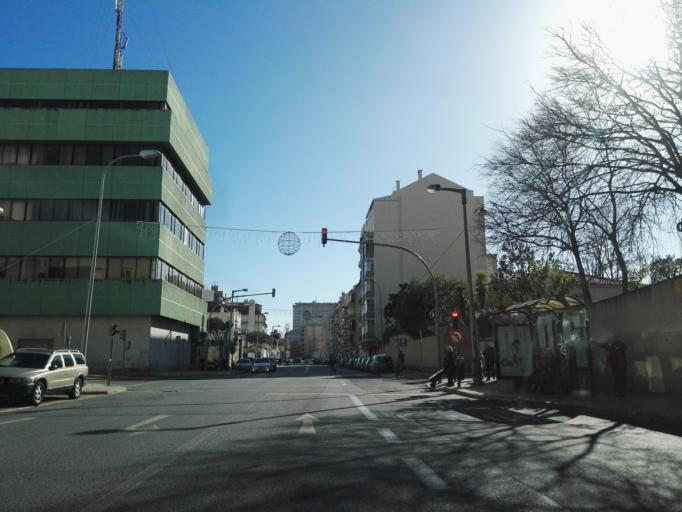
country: PT
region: Lisbon
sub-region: Odivelas
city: Olival do Basto
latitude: 38.7655
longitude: -9.1573
